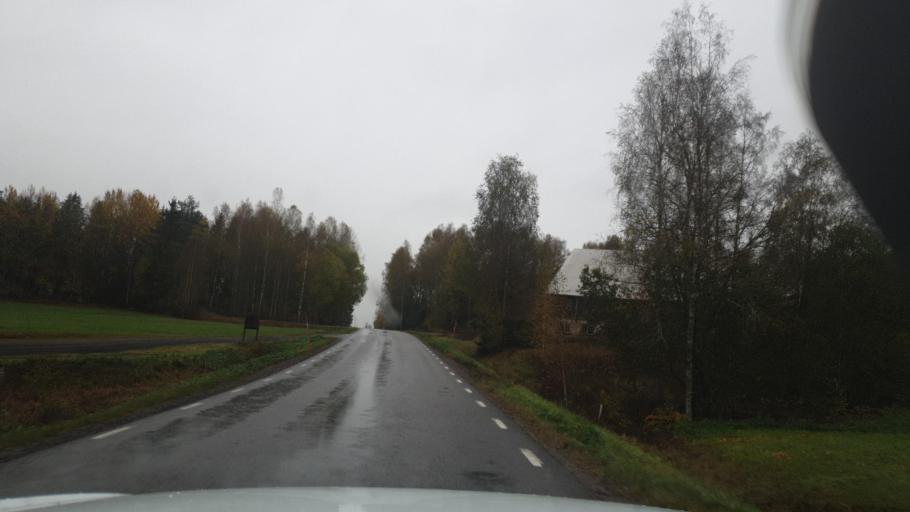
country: SE
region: Vaermland
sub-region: Eda Kommun
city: Charlottenberg
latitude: 59.7914
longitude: 12.1547
